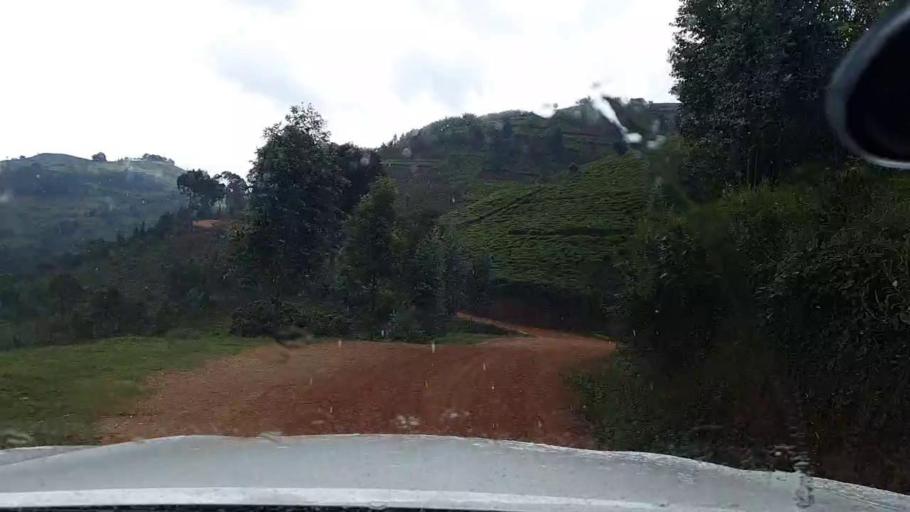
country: RW
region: Western Province
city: Kibuye
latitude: -2.1507
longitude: 29.4282
